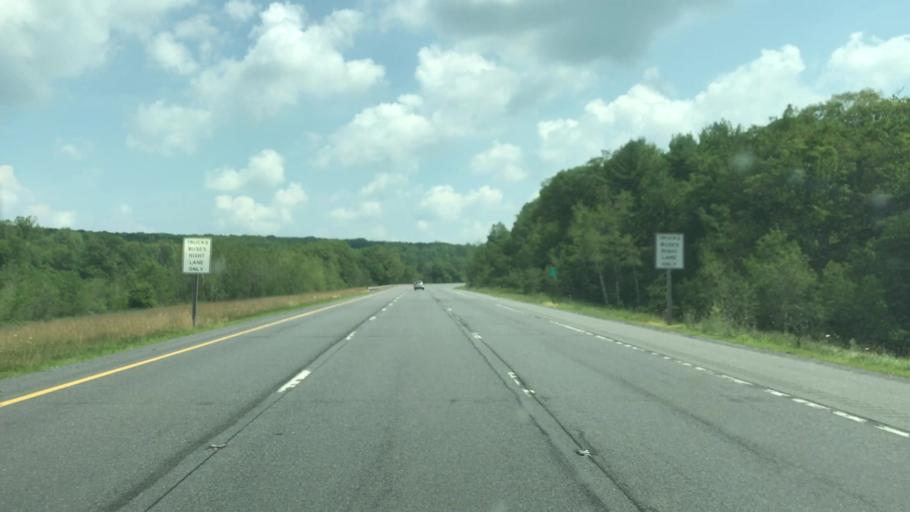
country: US
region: Pennsylvania
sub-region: Lackawanna County
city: Mount Cobb
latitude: 41.3940
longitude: -75.5439
